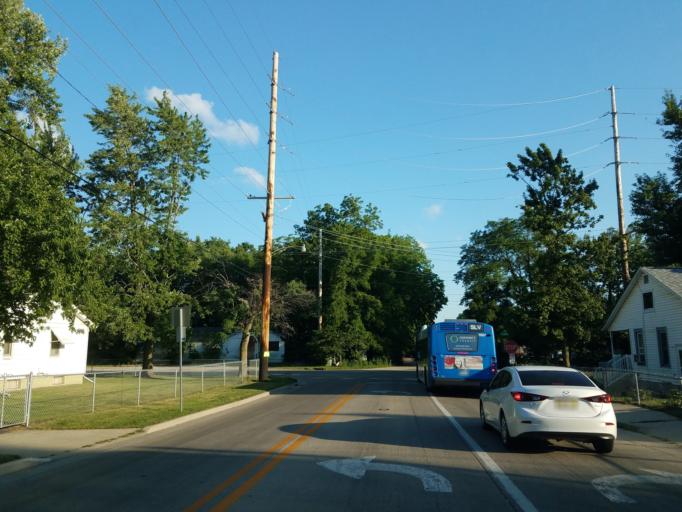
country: US
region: Illinois
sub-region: McLean County
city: Bloomington
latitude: 40.4737
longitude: -89.0163
